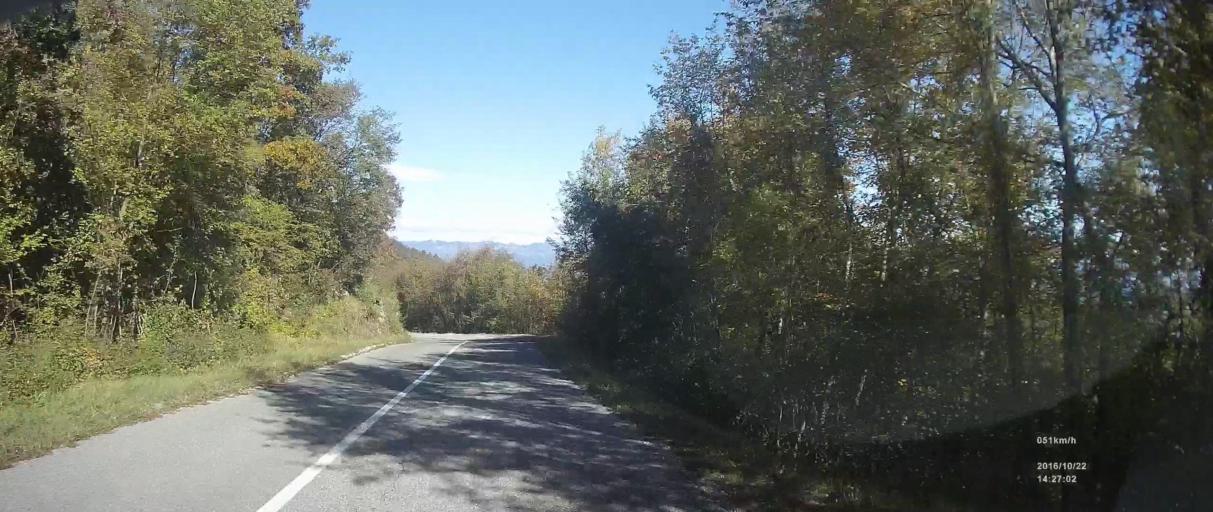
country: HR
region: Istarska
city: Lovran
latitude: 45.3197
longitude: 14.2370
